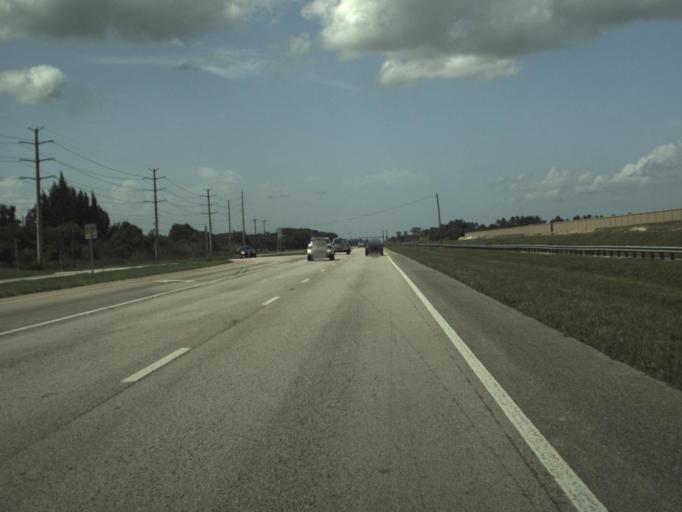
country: US
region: Florida
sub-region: Palm Beach County
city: Villages of Oriole
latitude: 26.4304
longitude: -80.2042
